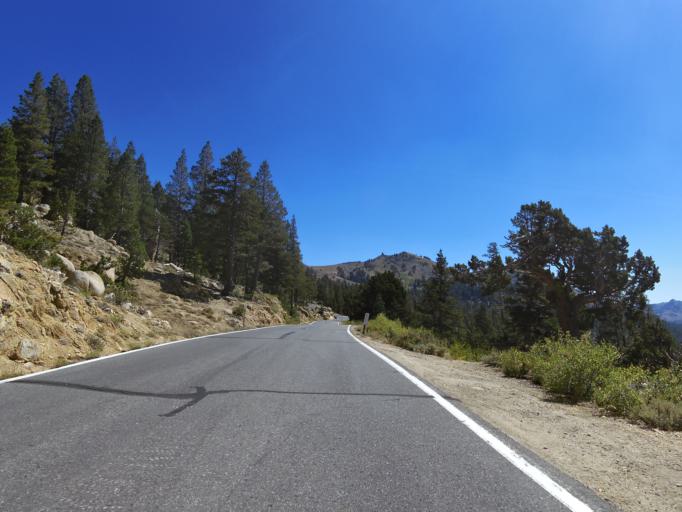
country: US
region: Nevada
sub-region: Douglas County
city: Gardnerville Ranchos
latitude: 38.5442
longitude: -119.8207
